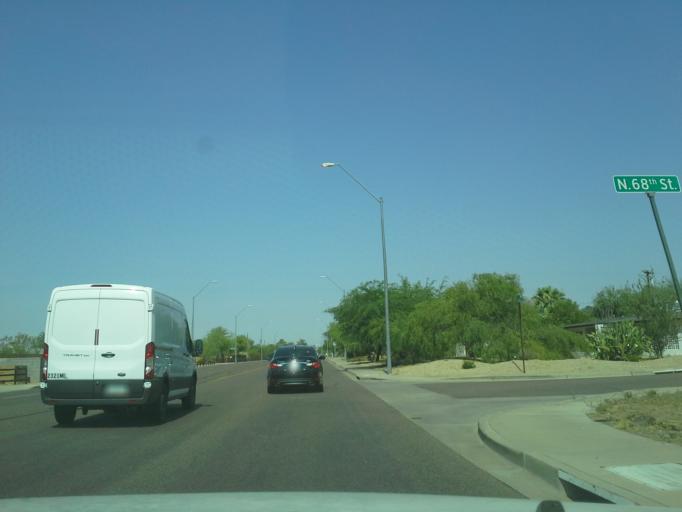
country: US
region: Arizona
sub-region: Maricopa County
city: Paradise Valley
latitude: 33.5968
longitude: -111.9358
